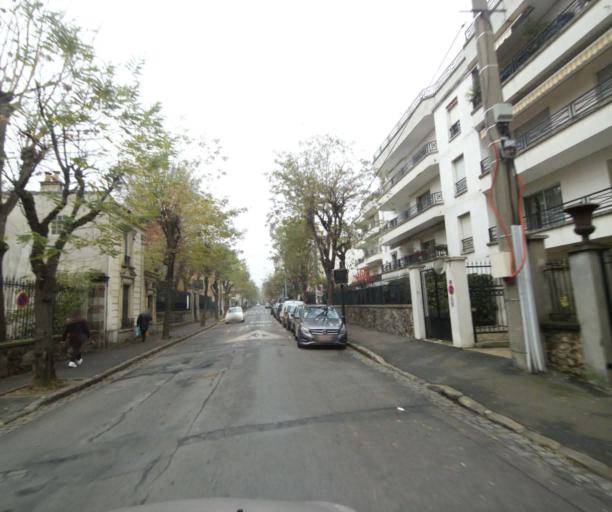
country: FR
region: Ile-de-France
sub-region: Departement de Seine-Saint-Denis
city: Le Raincy
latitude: 48.8912
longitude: 2.5113
